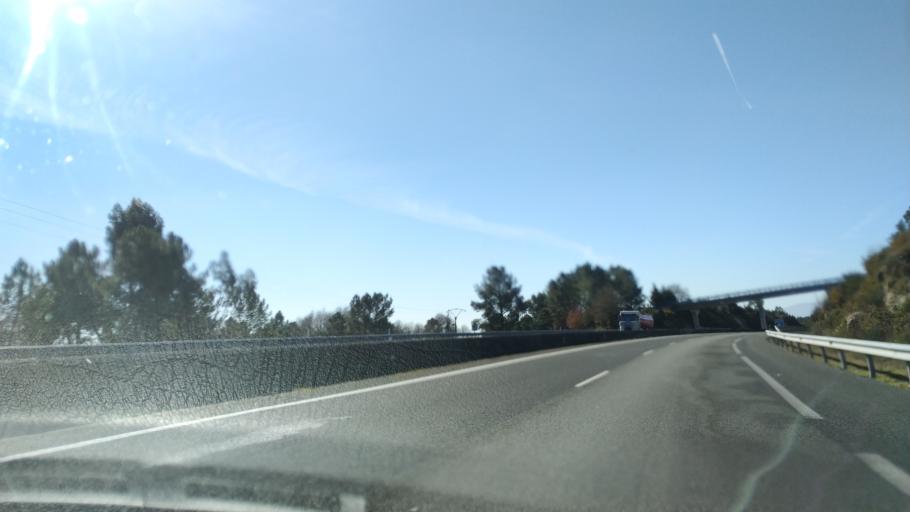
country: ES
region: Galicia
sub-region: Provincia de Ourense
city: Pinor
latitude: 42.5056
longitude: -8.0239
